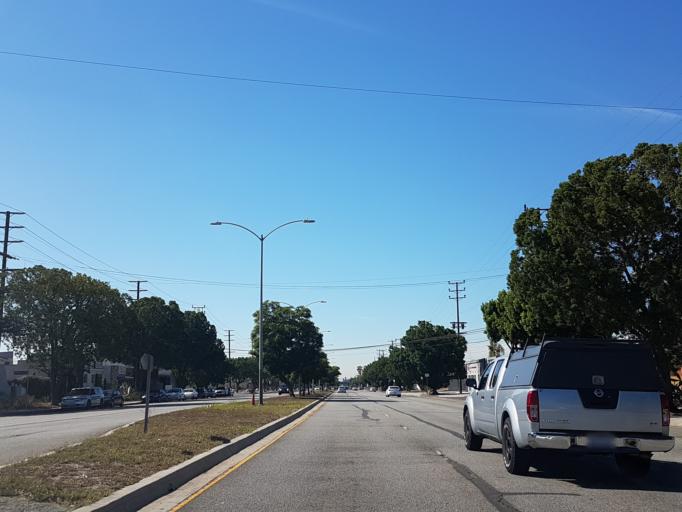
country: US
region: California
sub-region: Los Angeles County
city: Culver City
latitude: 34.0423
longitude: -118.3656
